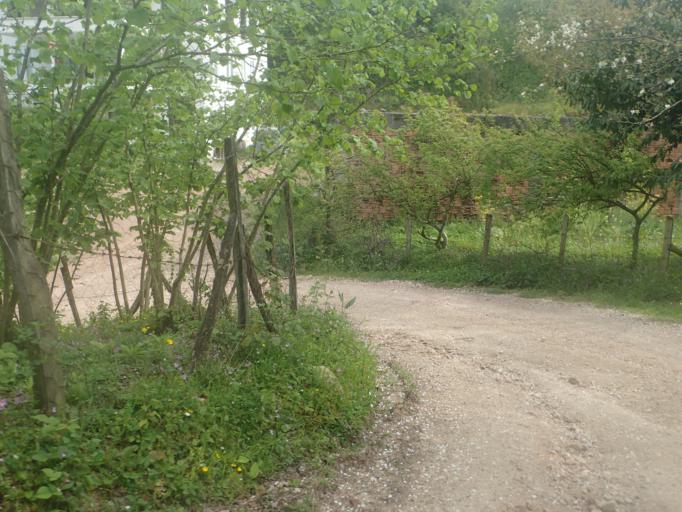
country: TR
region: Ordu
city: Catalpinar
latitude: 40.8996
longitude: 37.4851
